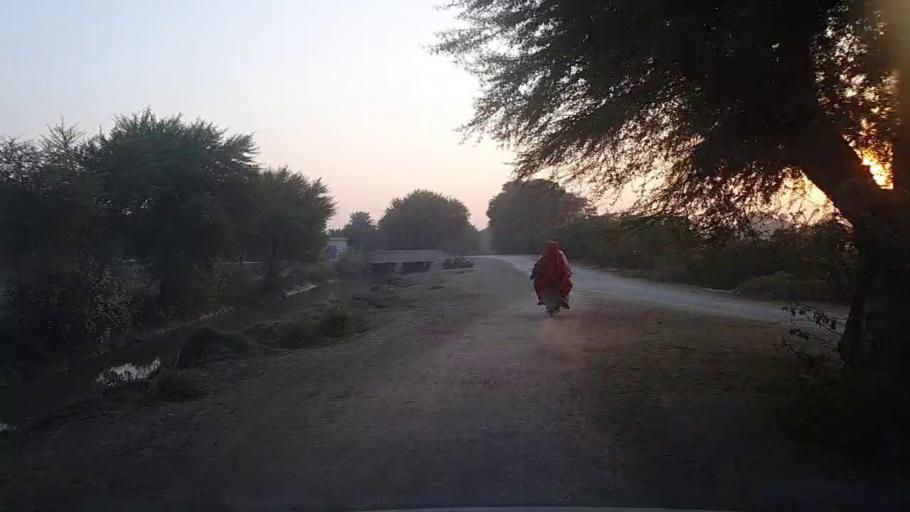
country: PK
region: Sindh
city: Karaundi
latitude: 26.8310
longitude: 68.3651
